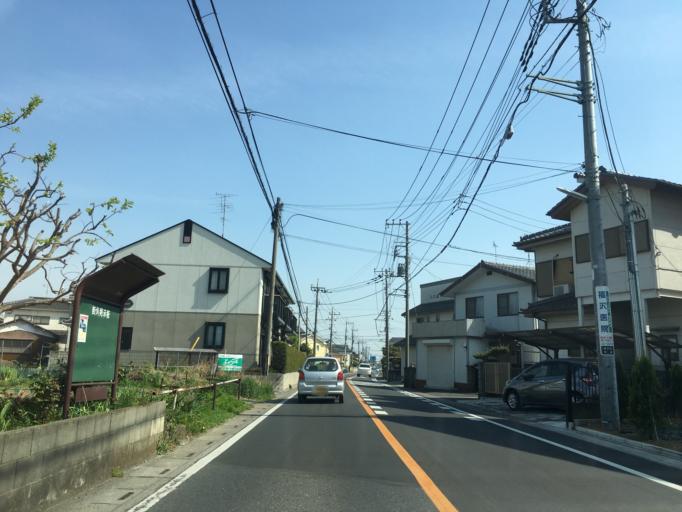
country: JP
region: Saitama
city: Sugito
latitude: 36.0216
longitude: 139.7327
